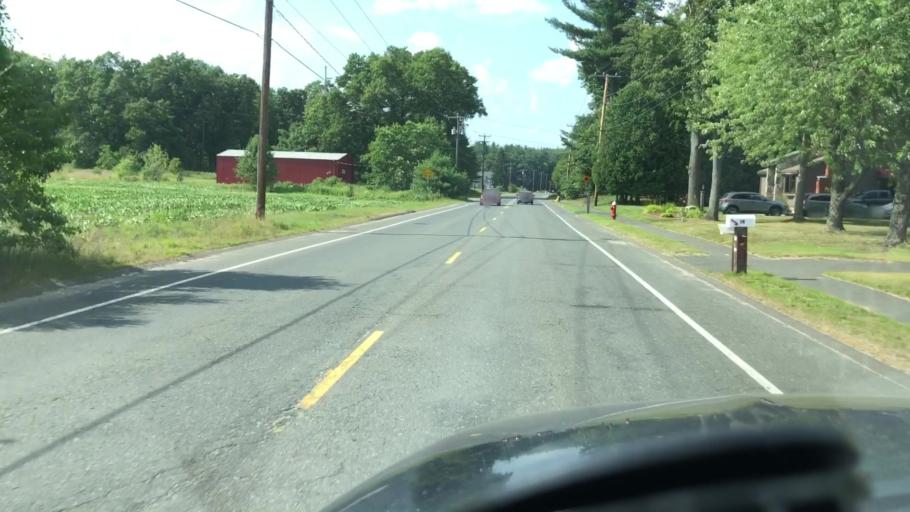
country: US
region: Massachusetts
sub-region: Hampshire County
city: Southampton
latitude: 42.2116
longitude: -72.6902
